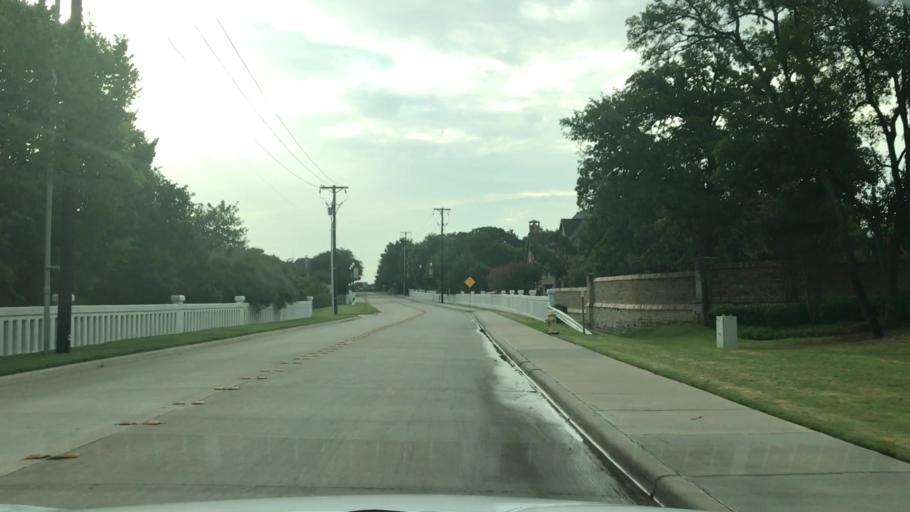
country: US
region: Texas
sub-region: Dallas County
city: Coppell
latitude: 32.9546
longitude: -96.9988
